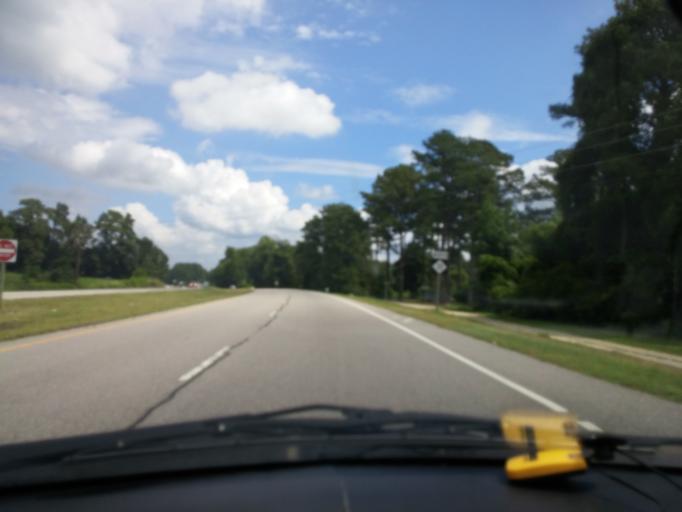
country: US
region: North Carolina
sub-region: Pitt County
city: Grifton
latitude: 35.3269
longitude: -77.4942
